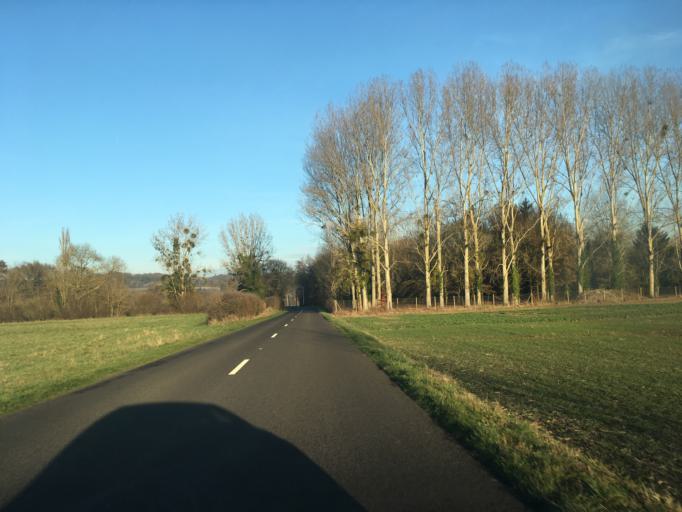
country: FR
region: Haute-Normandie
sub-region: Departement de l'Eure
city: Menilles
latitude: 49.0519
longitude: 1.3197
